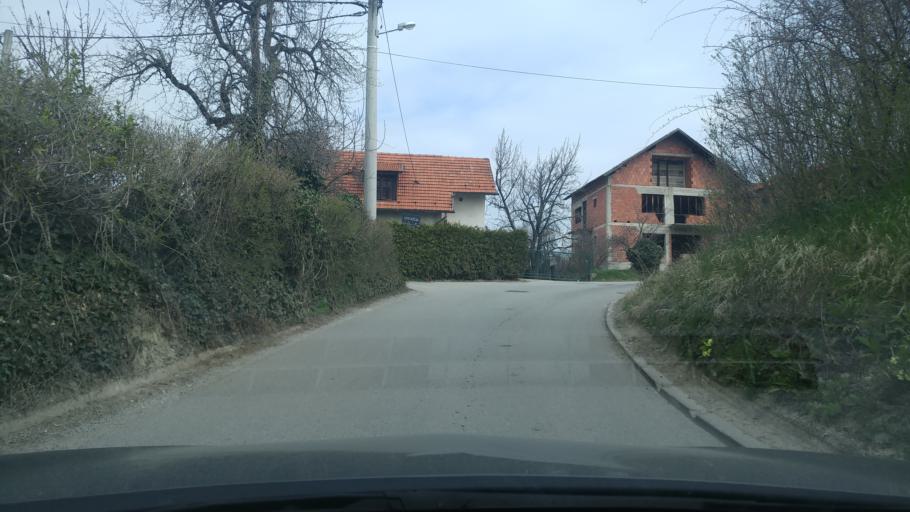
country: HR
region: Grad Zagreb
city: Stenjevec
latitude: 45.8423
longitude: 15.9249
